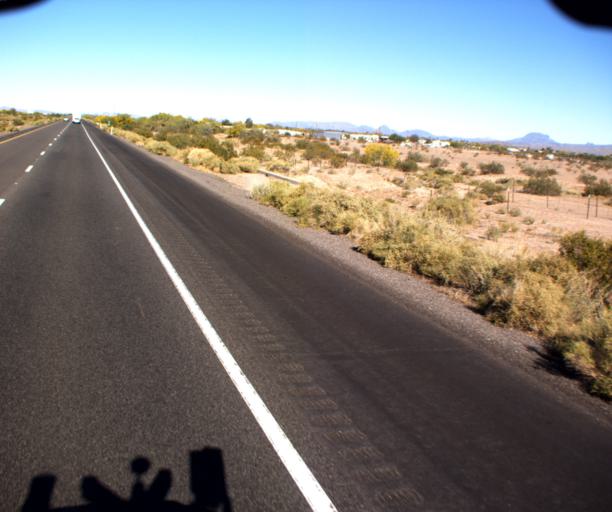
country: US
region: Arizona
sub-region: Maricopa County
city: Gila Bend
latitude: 32.9302
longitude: -112.6931
